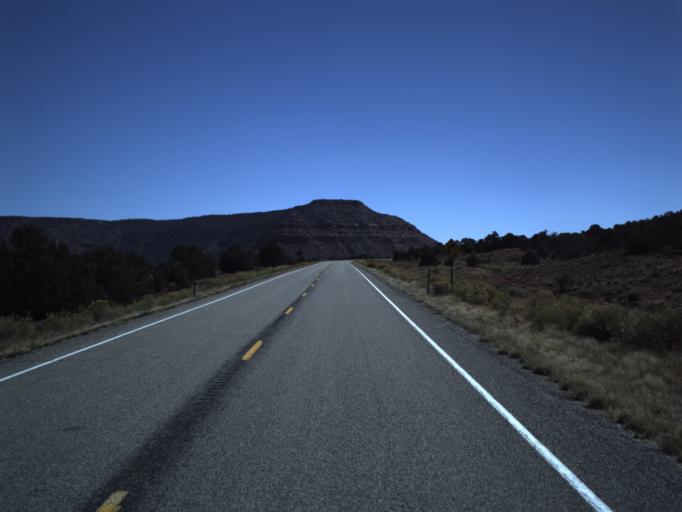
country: US
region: Utah
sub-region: San Juan County
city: Blanding
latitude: 37.6334
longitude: -110.0966
